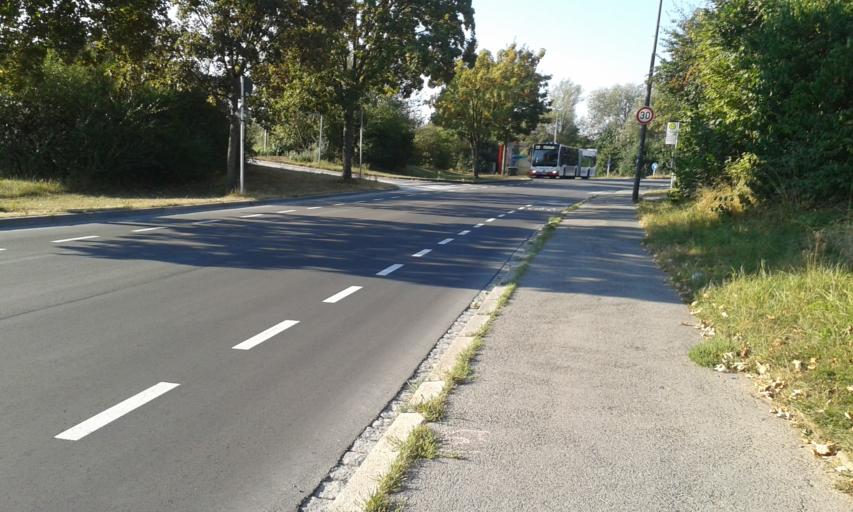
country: DE
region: Bavaria
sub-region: Upper Franconia
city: Bamberg
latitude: 49.8742
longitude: 10.8824
